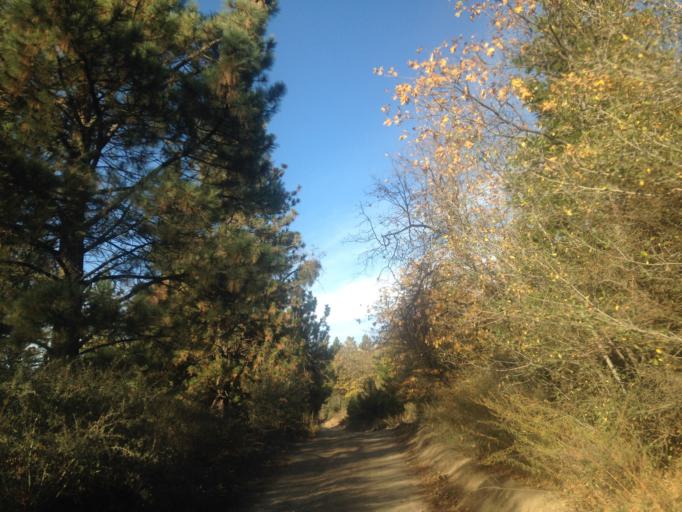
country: US
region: California
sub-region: San Bernardino County
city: Yucaipa
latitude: 34.1342
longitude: -117.0110
